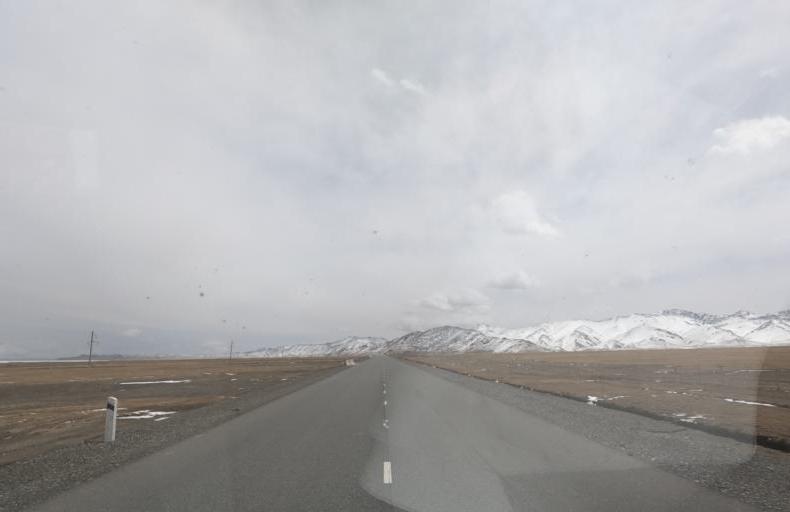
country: KG
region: Naryn
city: Baetov
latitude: 40.5515
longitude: 75.2255
